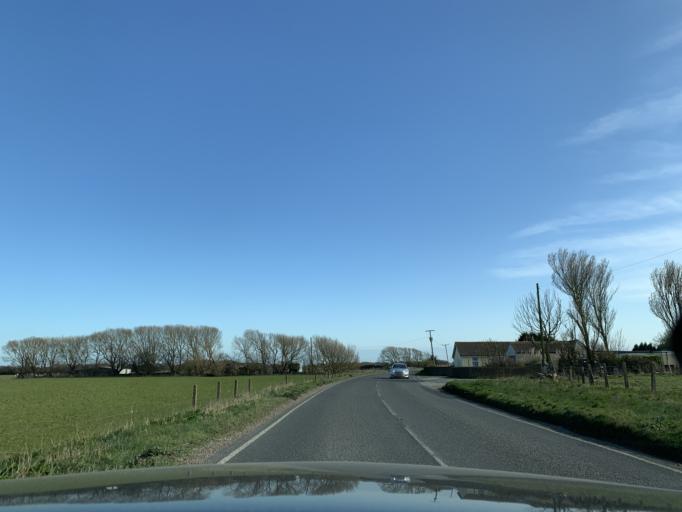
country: GB
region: England
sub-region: Kent
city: Lydd
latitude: 50.9448
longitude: 0.9267
